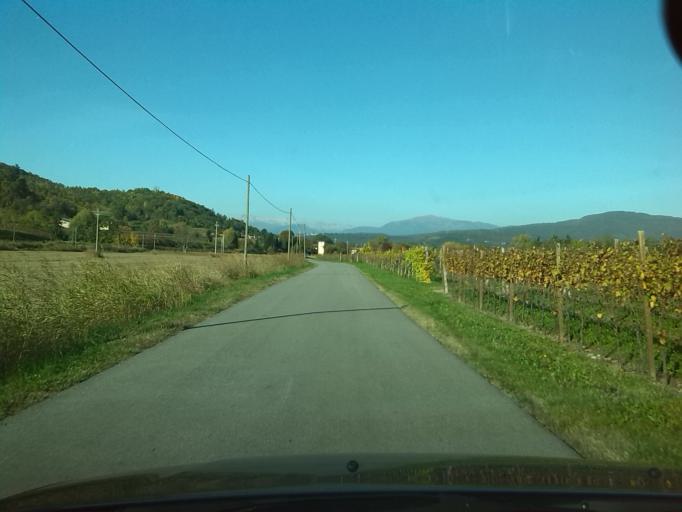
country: IT
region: Friuli Venezia Giulia
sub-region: Provincia di Gorizia
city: Dolegna del Collio
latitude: 46.0262
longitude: 13.4749
